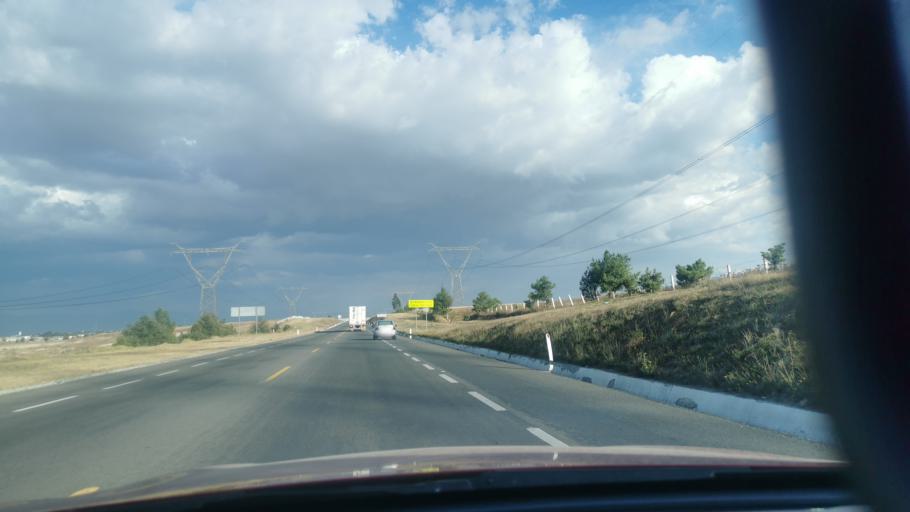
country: MX
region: Mexico
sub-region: Almoloya de Juarez
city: El Plan
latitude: 19.3828
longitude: -99.7890
